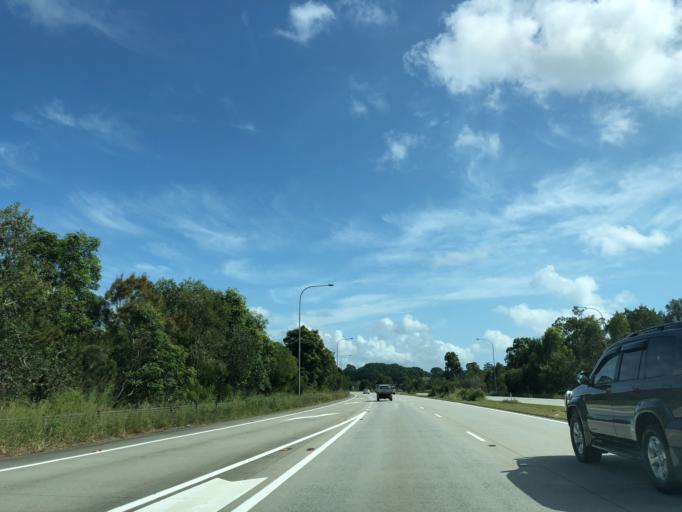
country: AU
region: New South Wales
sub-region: Byron Shire
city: Brunswick Heads
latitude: -28.5817
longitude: 153.5445
